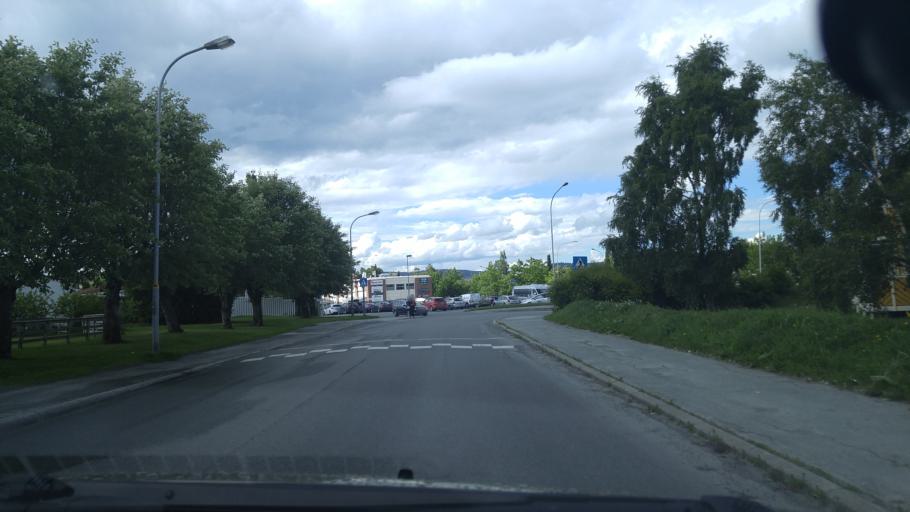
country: NO
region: Sor-Trondelag
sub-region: Trondheim
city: Trondheim
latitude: 63.4039
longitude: 10.4297
